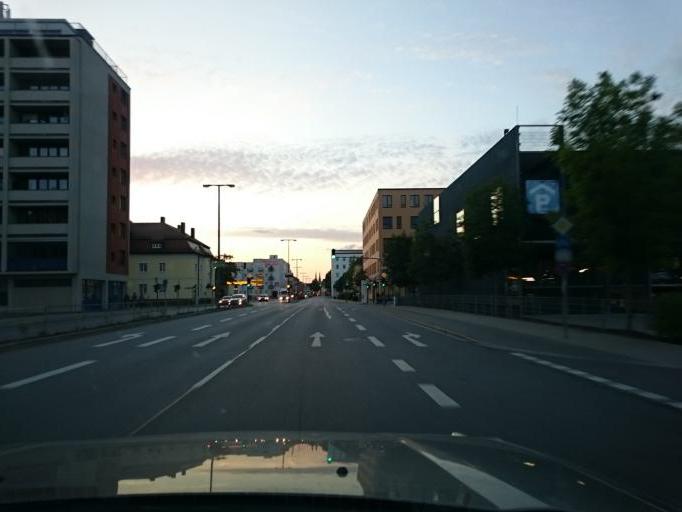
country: DE
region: Bavaria
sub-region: Upper Palatinate
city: Regensburg
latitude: 49.0051
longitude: 12.1200
